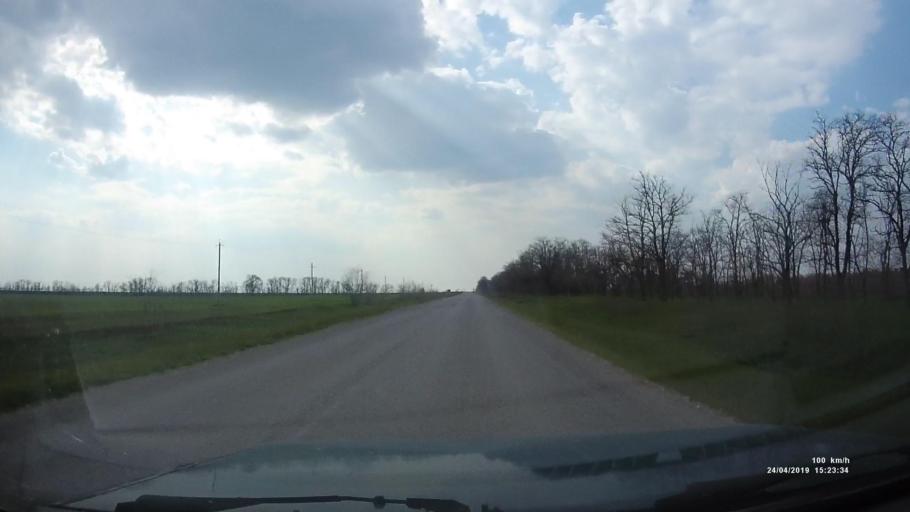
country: RU
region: Rostov
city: Remontnoye
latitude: 46.5446
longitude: 43.0864
